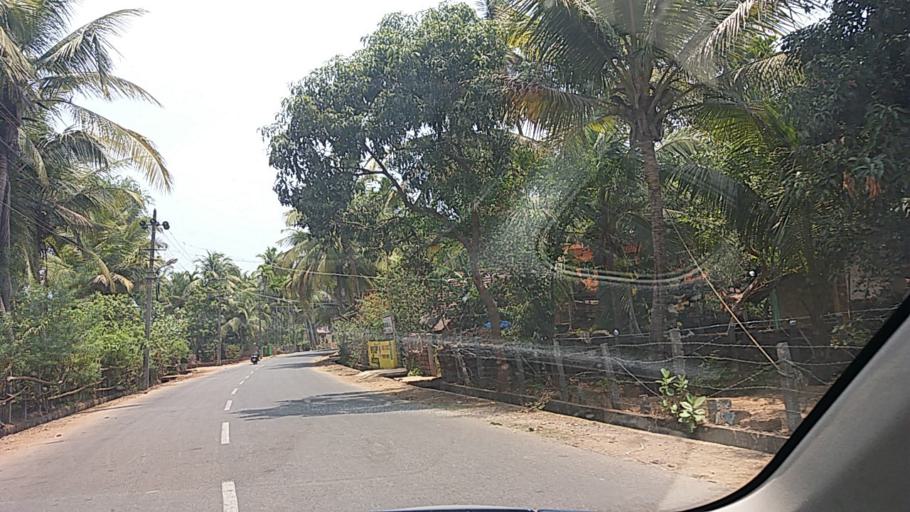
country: IN
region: Karnataka
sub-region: Uttar Kannada
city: Karwar
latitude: 14.8140
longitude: 74.1522
